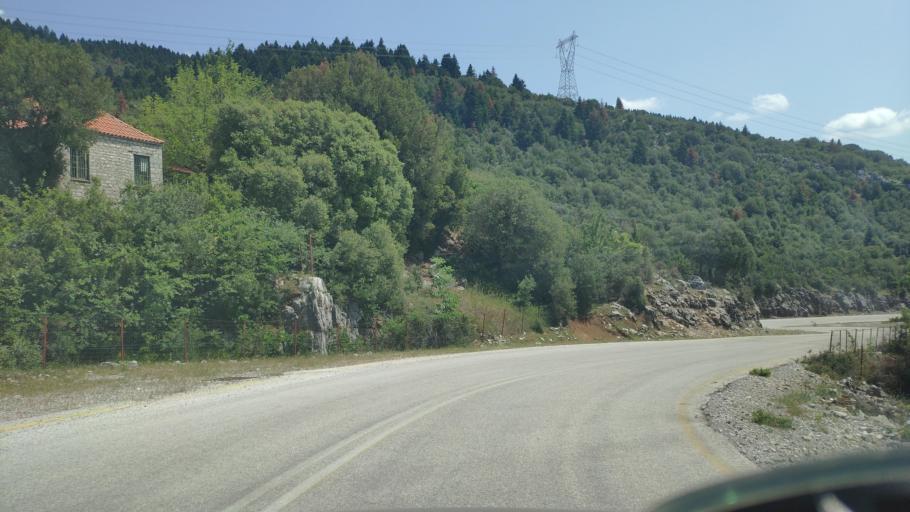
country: GR
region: Epirus
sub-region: Nomos Artas
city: Ano Kalentini
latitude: 39.2610
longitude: 21.2502
